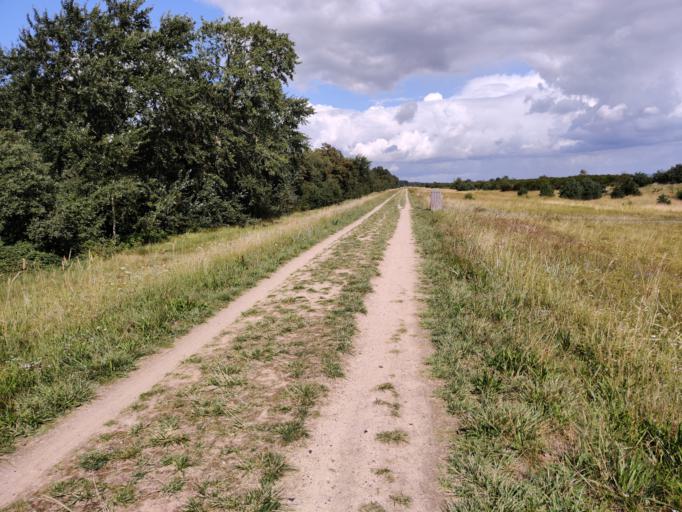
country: DK
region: Zealand
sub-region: Guldborgsund Kommune
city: Nykobing Falster
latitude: 54.6049
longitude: 11.9670
